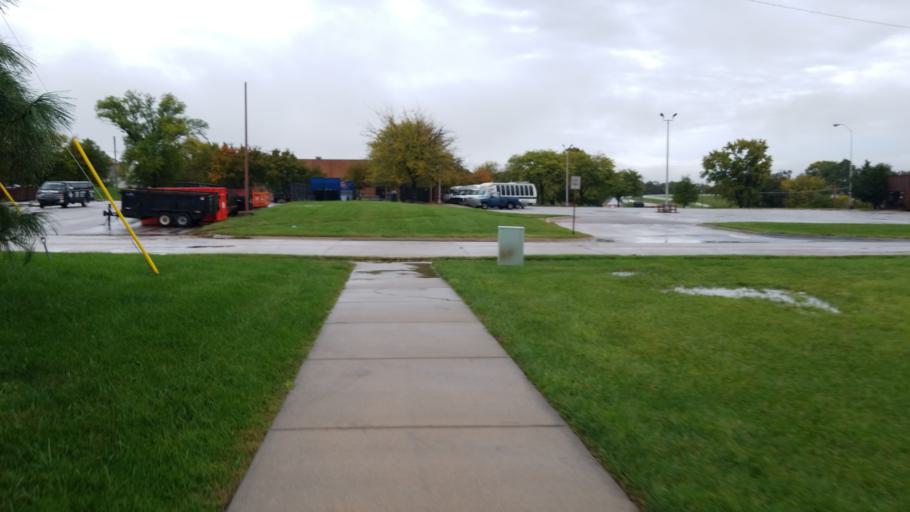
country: US
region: Nebraska
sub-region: Sarpy County
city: Offutt Air Force Base
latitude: 41.1265
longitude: -95.9489
